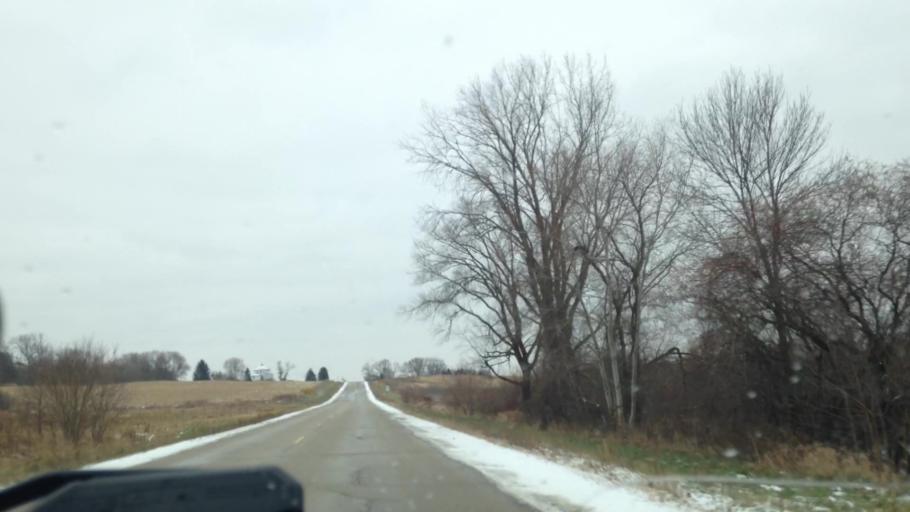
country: US
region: Wisconsin
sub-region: Dodge County
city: Mayville
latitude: 43.4478
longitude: -88.5001
